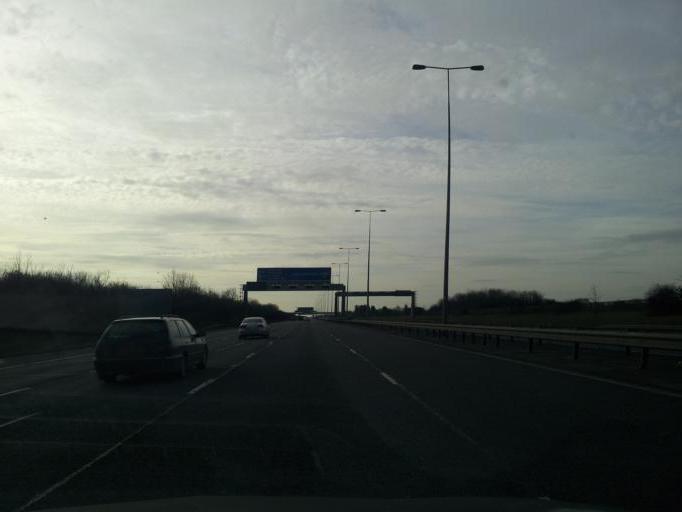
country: GB
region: England
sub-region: Cambridgeshire
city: Sawtry
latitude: 52.3939
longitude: -0.2604
